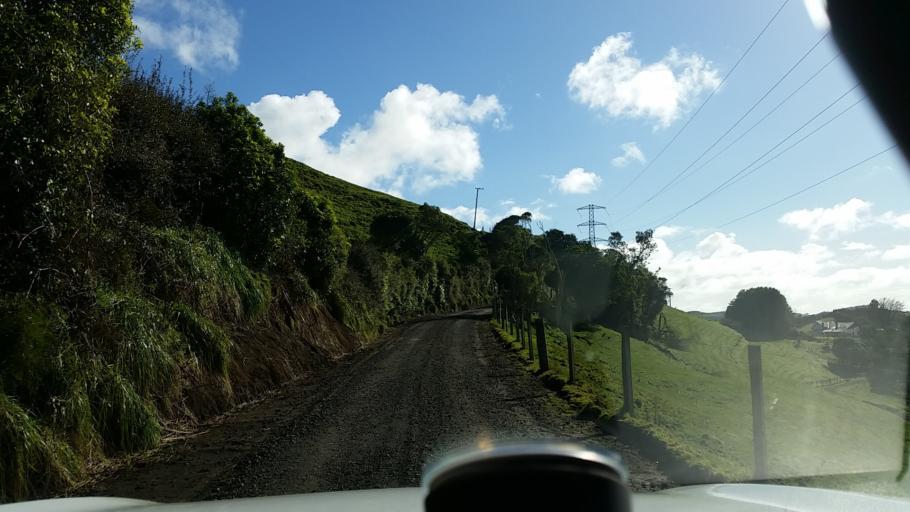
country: NZ
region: Taranaki
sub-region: South Taranaki District
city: Eltham
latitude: -39.4554
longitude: 174.3689
